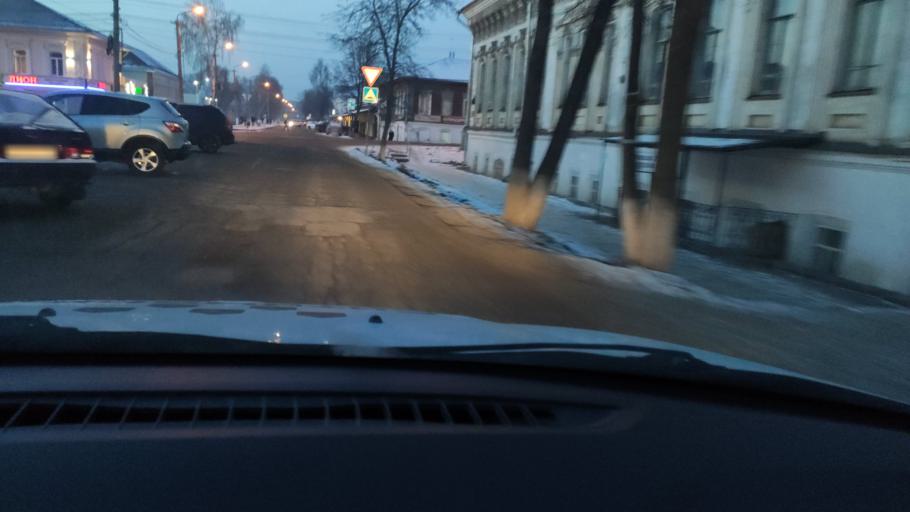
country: RU
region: Perm
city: Kungur
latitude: 57.4373
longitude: 56.9366
